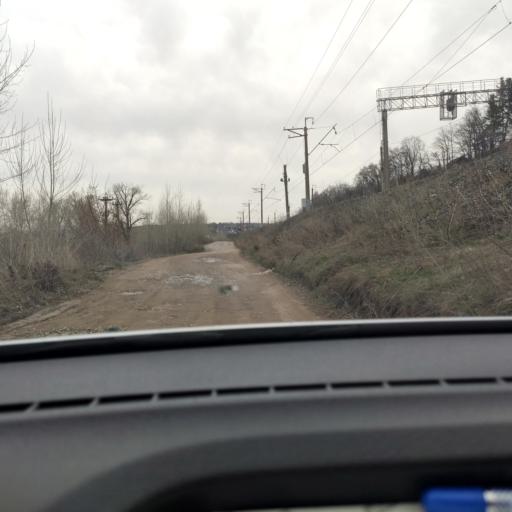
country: RU
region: Bashkortostan
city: Avdon
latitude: 54.6090
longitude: 55.6087
